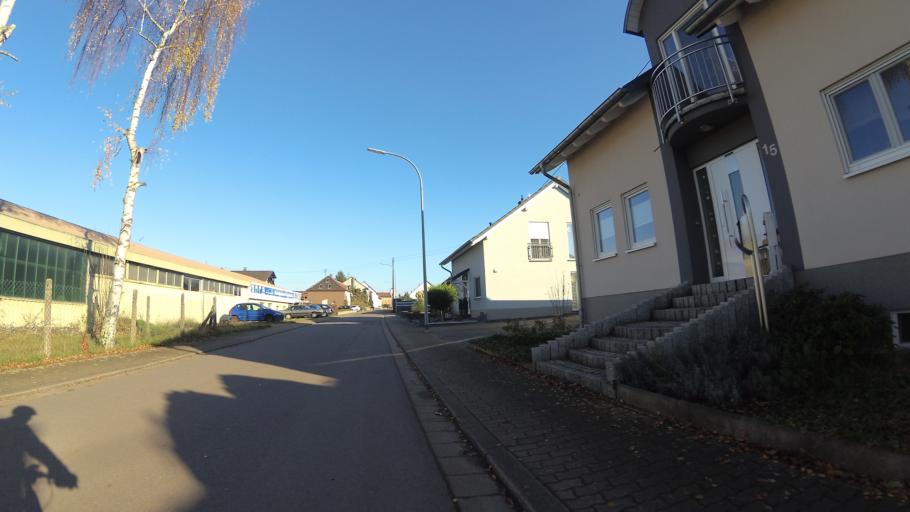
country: DE
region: Saarland
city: Ensdorf
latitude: 49.2965
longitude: 6.7963
